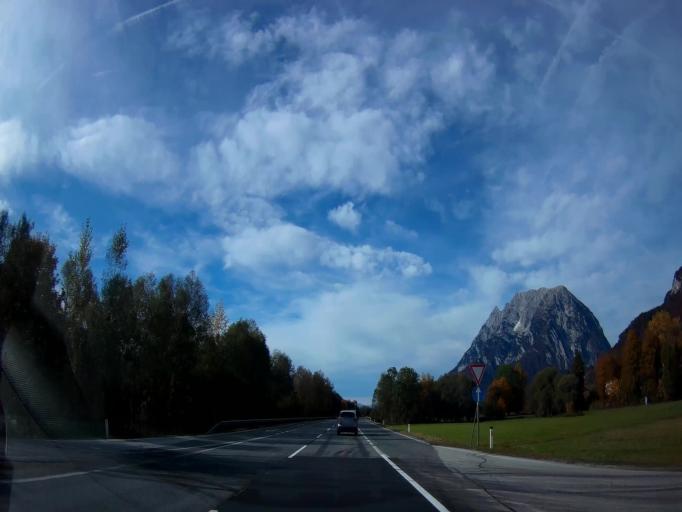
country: AT
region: Styria
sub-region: Politischer Bezirk Liezen
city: Stainach
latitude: 47.5281
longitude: 14.1168
